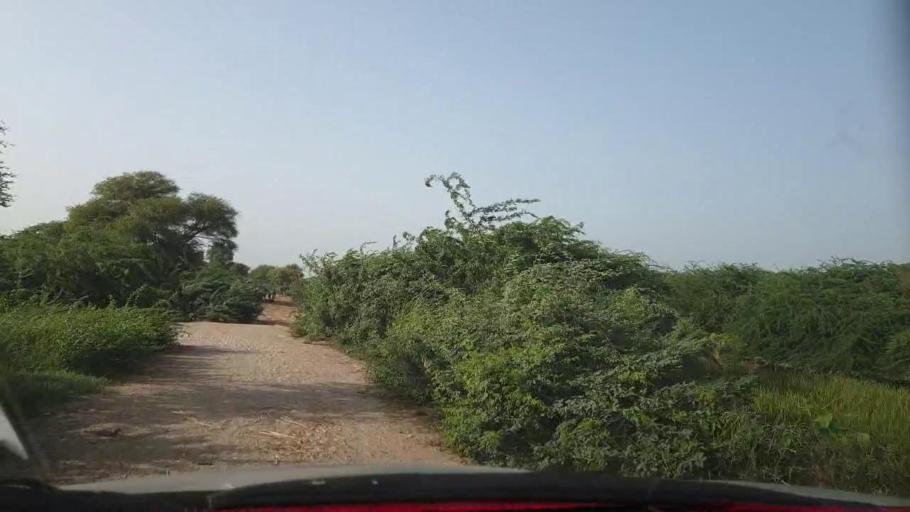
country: PK
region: Sindh
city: Talhar
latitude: 24.8977
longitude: 68.8196
